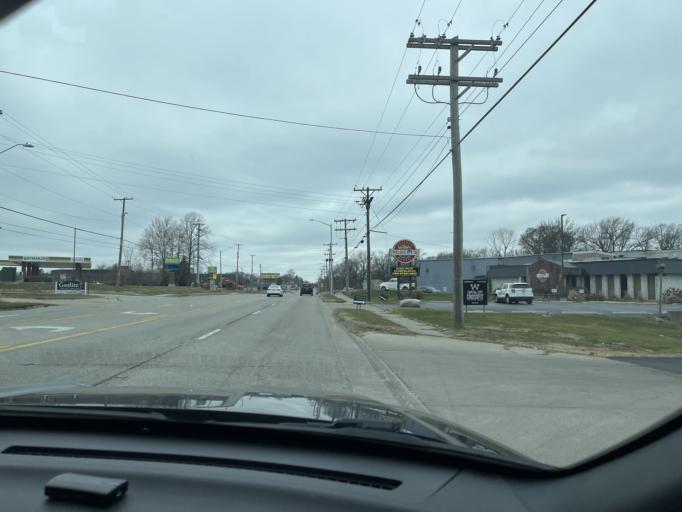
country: US
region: Illinois
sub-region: Sangamon County
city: Leland Grove
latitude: 39.8076
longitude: -89.6800
